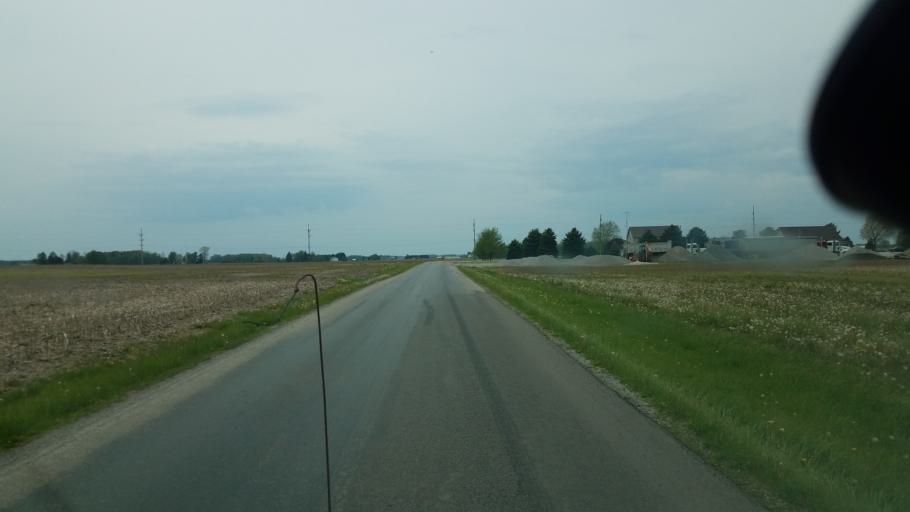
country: US
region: Ohio
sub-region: Richland County
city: Shelby
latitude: 40.8944
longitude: -82.6825
